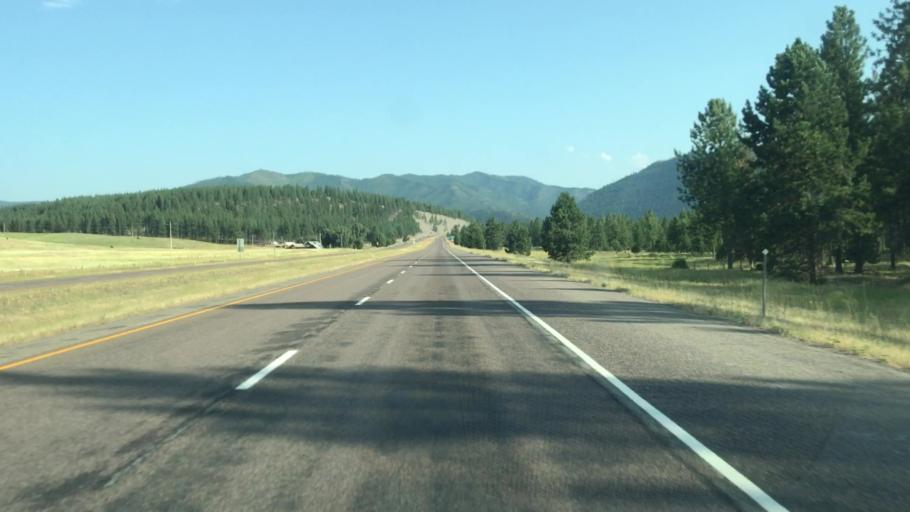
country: US
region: Montana
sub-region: Mineral County
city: Superior
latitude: 47.0342
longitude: -114.7450
